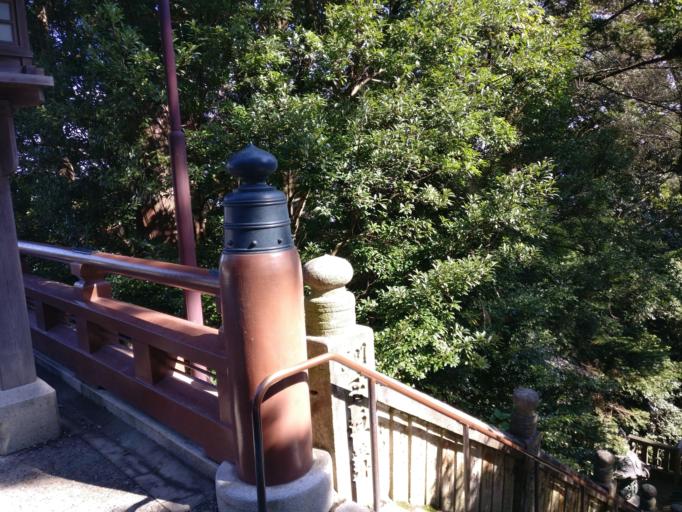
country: JP
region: Kagawa
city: Marugame
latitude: 34.1842
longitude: 133.8098
